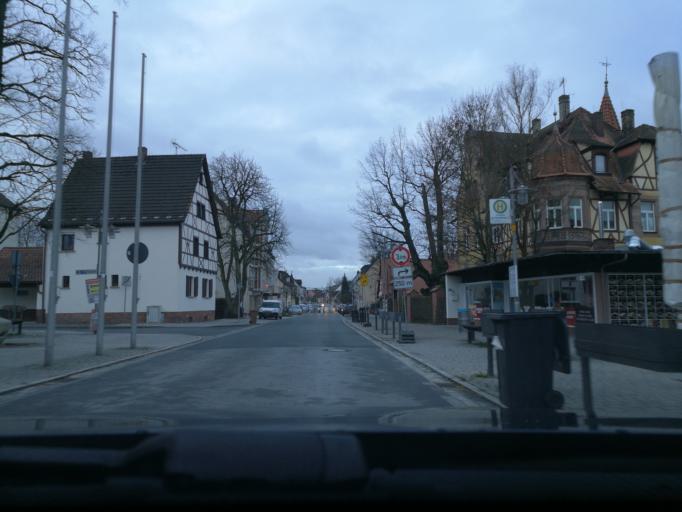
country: DE
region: Bavaria
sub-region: Regierungsbezirk Mittelfranken
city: Heroldsberg
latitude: 49.5334
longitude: 11.1528
